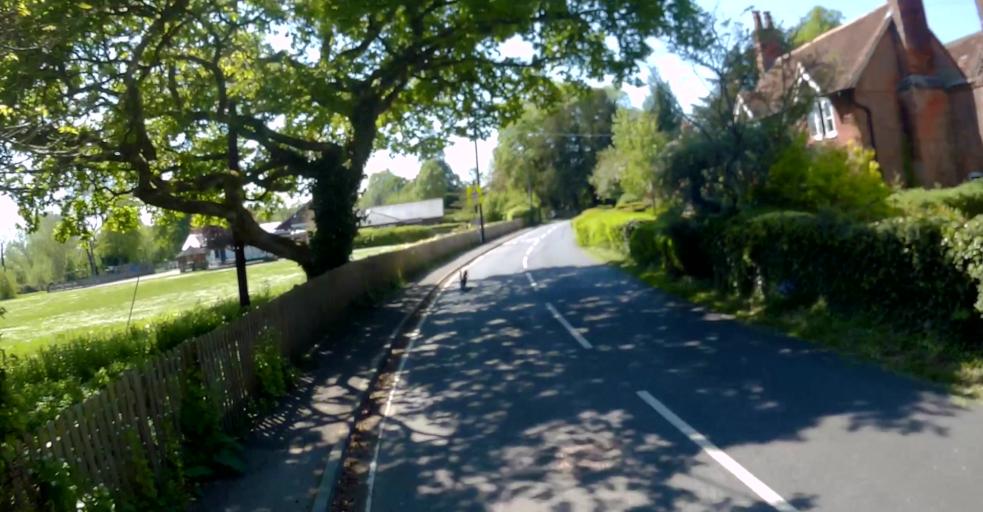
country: GB
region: England
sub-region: Hampshire
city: Andover
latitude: 51.1937
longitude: -1.3900
